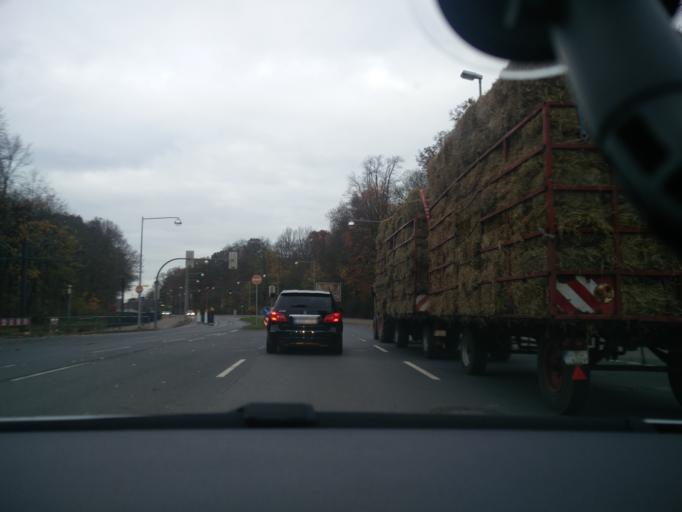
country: DE
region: Lower Saxony
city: Laatzen
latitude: 52.3583
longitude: 9.7906
